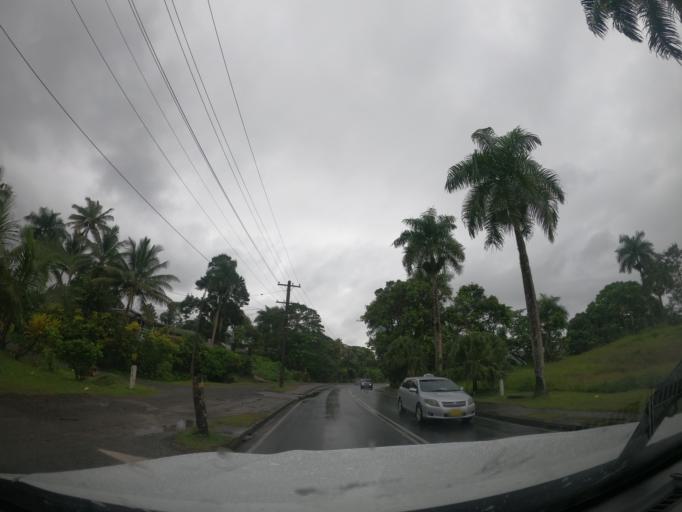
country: FJ
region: Central
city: Suva
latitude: -18.1130
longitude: 178.4216
